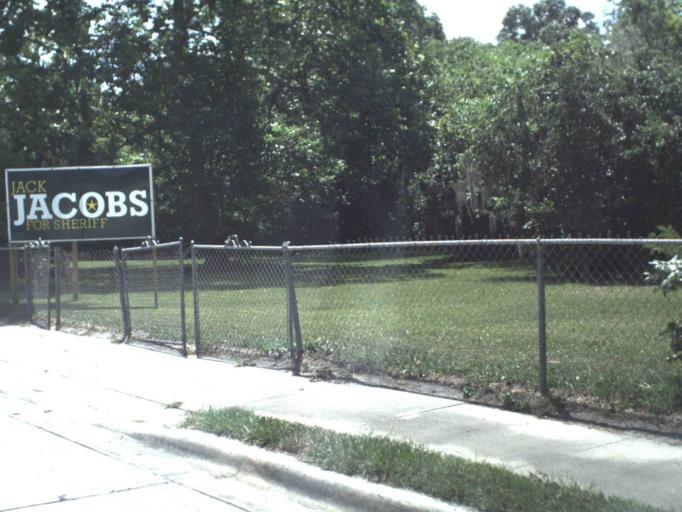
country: US
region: Florida
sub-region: Alachua County
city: Waldo
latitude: 29.7879
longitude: -82.1715
